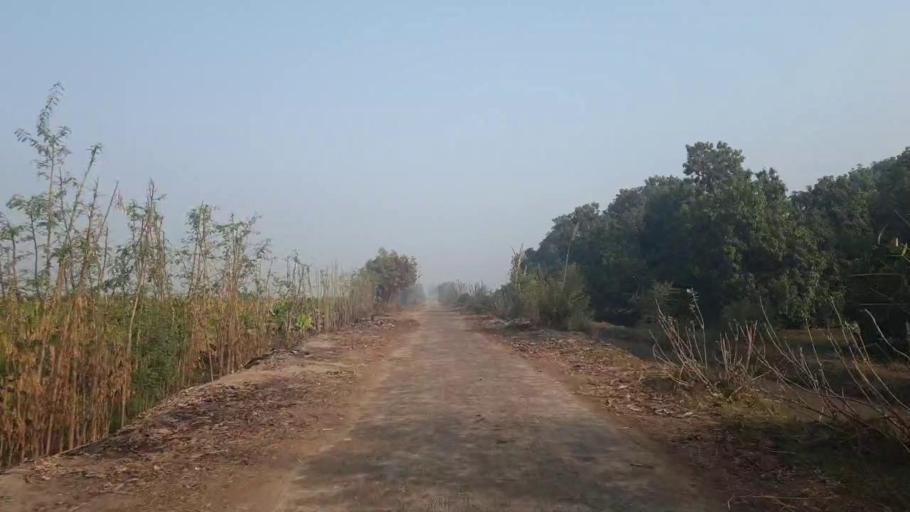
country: PK
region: Sindh
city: Tando Adam
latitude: 25.8143
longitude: 68.6323
